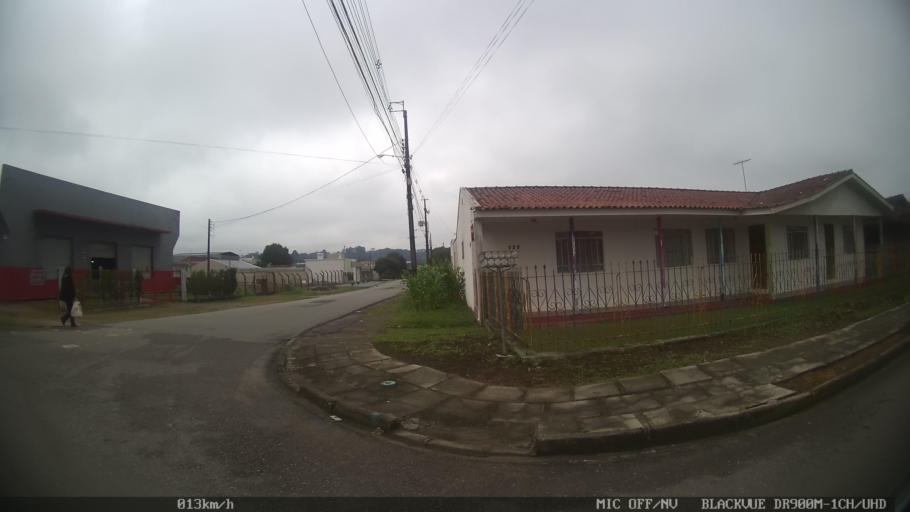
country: BR
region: Parana
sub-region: Sao Jose Dos Pinhais
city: Sao Jose dos Pinhais
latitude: -25.6020
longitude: -49.1708
